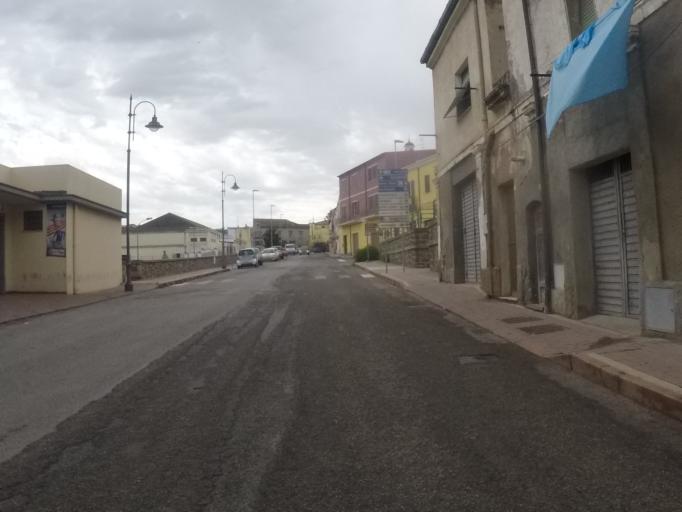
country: IT
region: Sardinia
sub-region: Provincia di Sassari
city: Sorso
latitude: 40.8014
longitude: 8.5807
